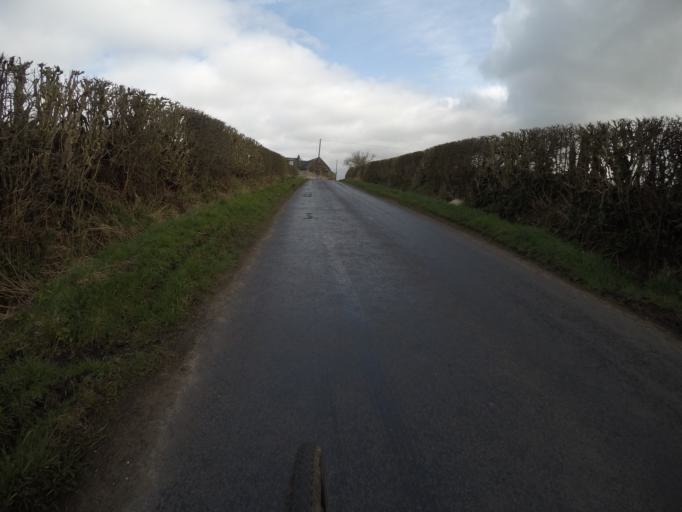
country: GB
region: Scotland
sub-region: North Ayrshire
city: Springside
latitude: 55.6610
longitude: -4.6074
